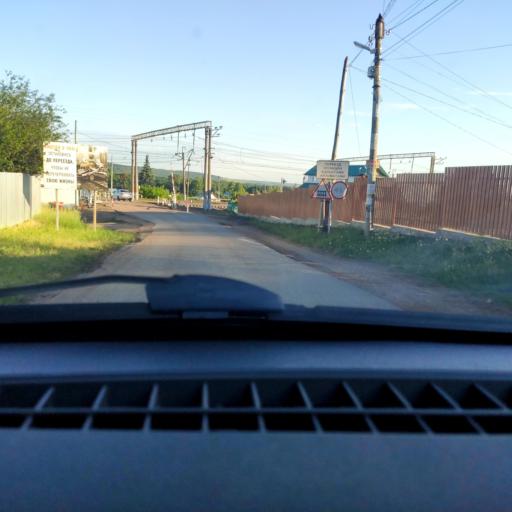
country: RU
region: Bashkortostan
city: Avdon
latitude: 54.6167
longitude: 55.6527
